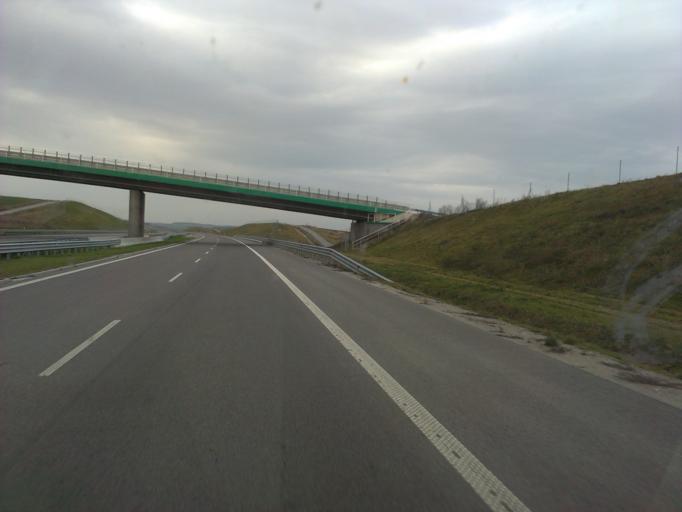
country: PL
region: Subcarpathian Voivodeship
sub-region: Powiat jaroslawski
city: Ostrow
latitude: 49.9303
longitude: 22.7163
